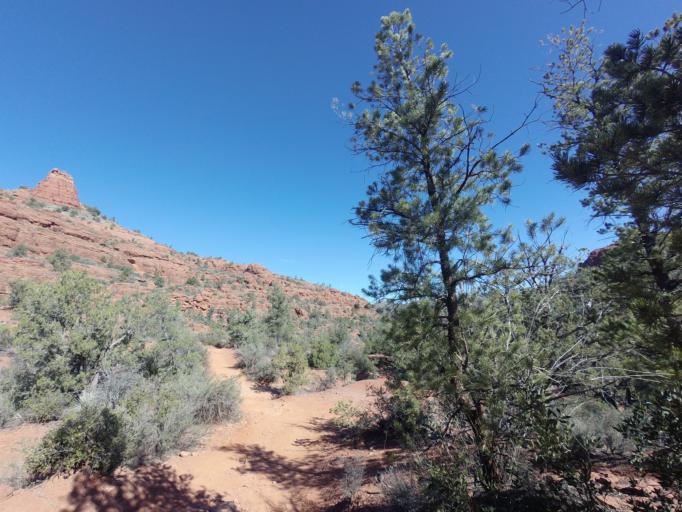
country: US
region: Arizona
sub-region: Yavapai County
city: West Sedona
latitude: 34.8174
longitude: -111.8007
